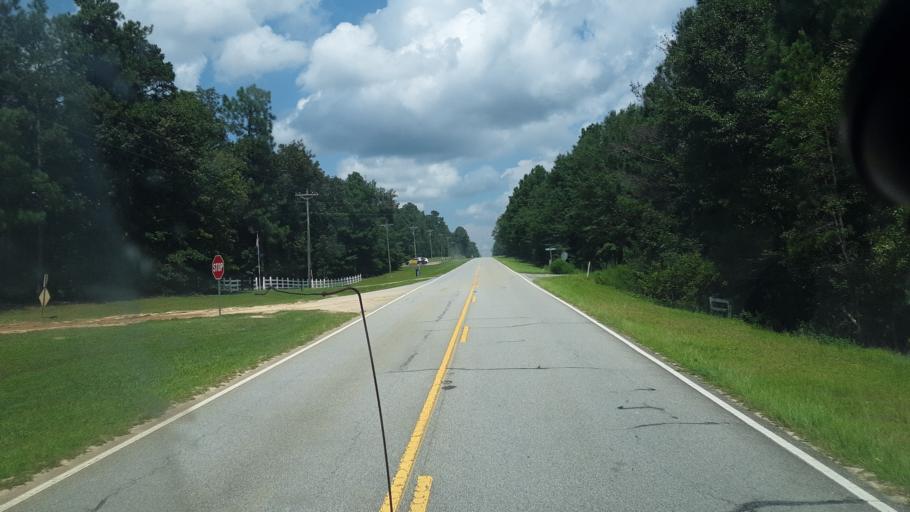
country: US
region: South Carolina
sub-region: Calhoun County
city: Oak Grove
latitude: 33.7450
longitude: -80.9601
